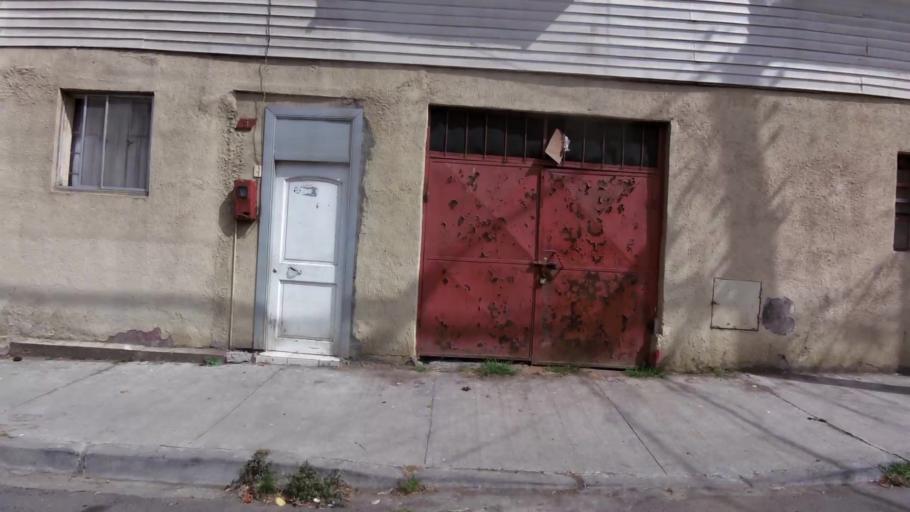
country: CL
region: Biobio
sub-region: Provincia de Concepcion
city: Talcahuano
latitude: -36.7179
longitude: -73.1183
